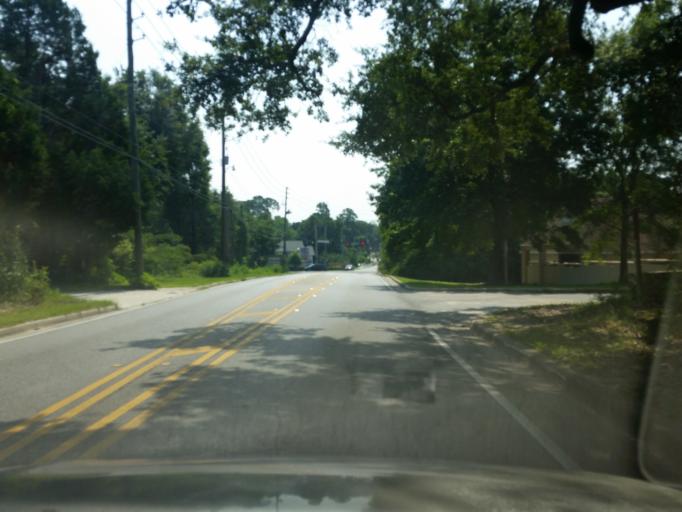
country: US
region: Florida
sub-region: Escambia County
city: Ferry Pass
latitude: 30.5180
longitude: -87.2223
